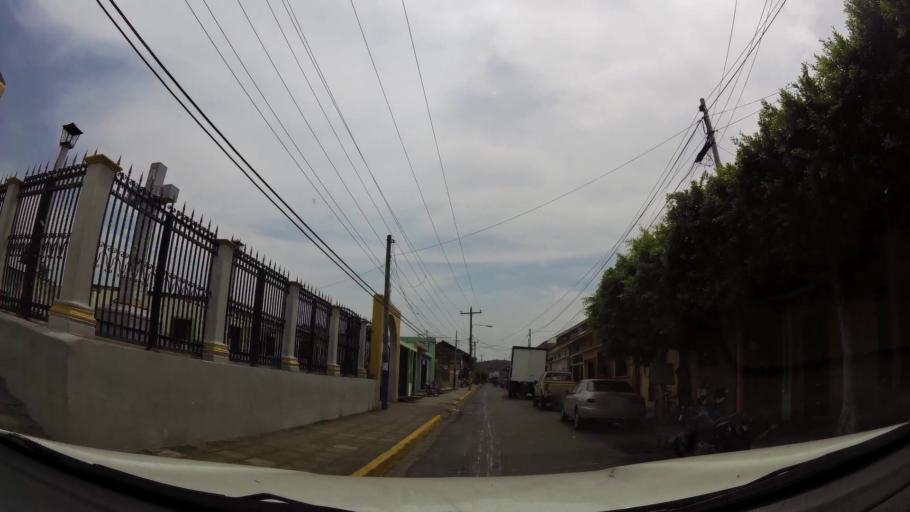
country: NI
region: Rivas
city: Rivas
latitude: 11.4377
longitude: -85.8314
